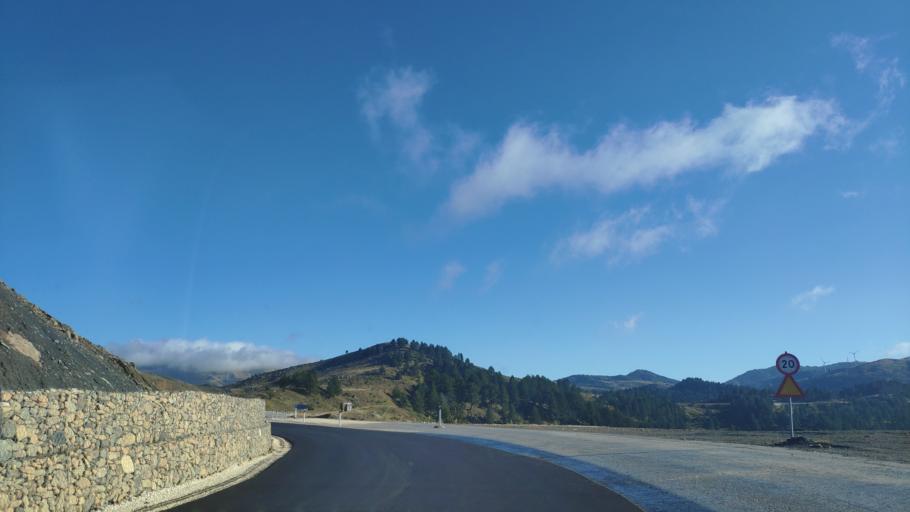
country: GR
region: Epirus
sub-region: Nomos Ioanninon
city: Metsovo
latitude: 39.7908
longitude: 21.1646
